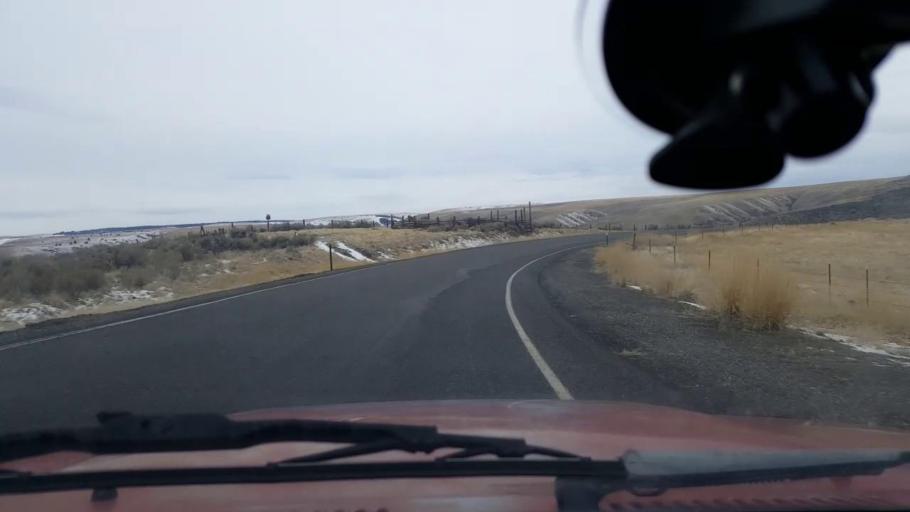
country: US
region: Washington
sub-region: Asotin County
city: Clarkston Heights-Vineland
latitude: 46.3122
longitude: -117.3403
